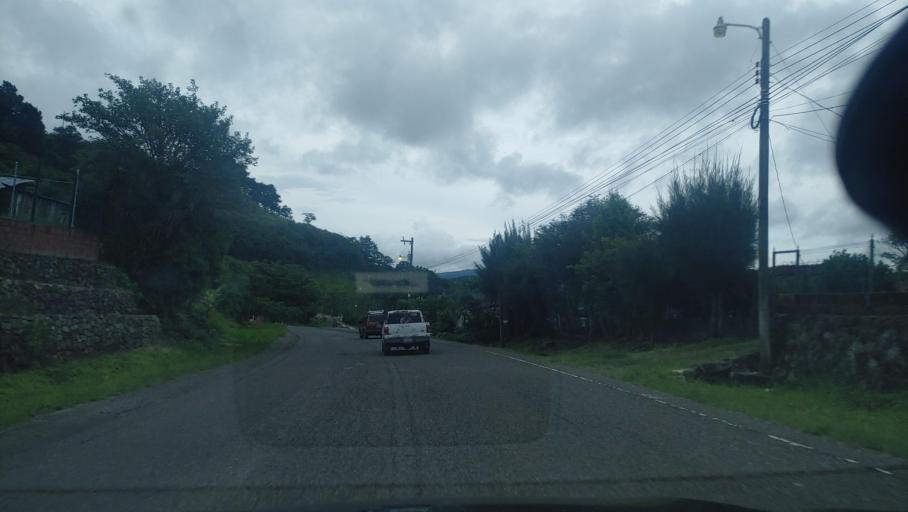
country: HN
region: Choluteca
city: San Marcos de Colon
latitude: 13.3758
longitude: -86.8918
